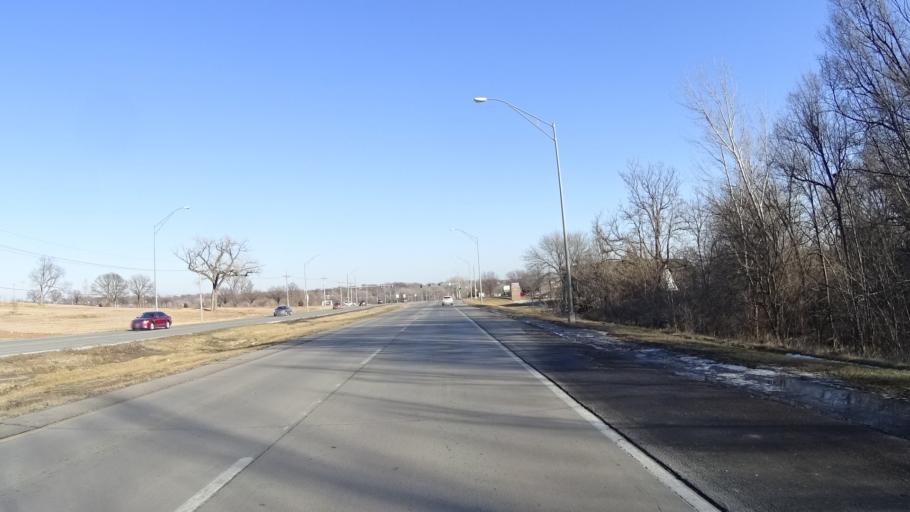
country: US
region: Nebraska
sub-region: Douglas County
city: Bennington
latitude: 41.2922
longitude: -96.1083
